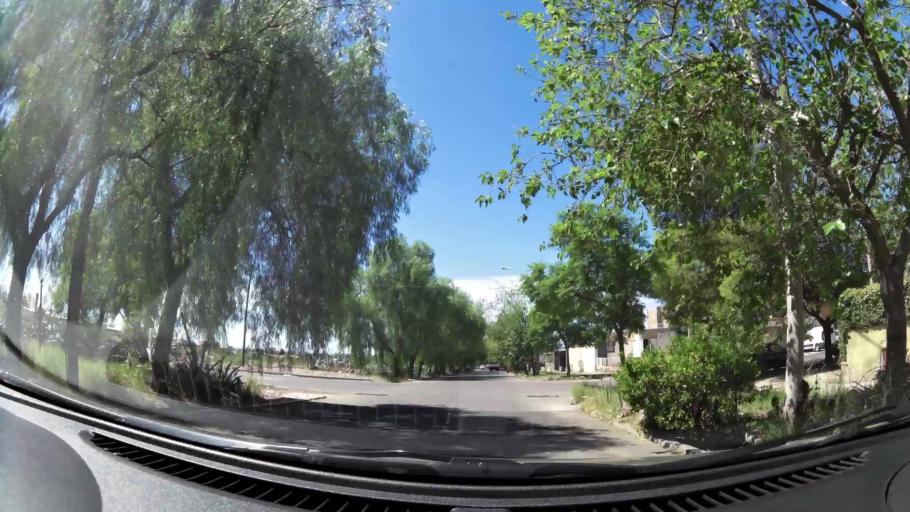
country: AR
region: Mendoza
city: Las Heras
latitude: -32.8414
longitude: -68.8682
